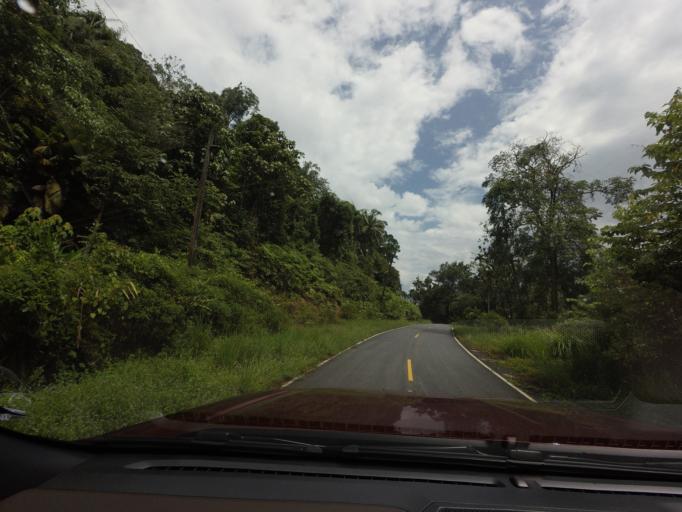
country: TH
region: Narathiwat
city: Sukhirin
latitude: 5.9413
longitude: 101.6525
